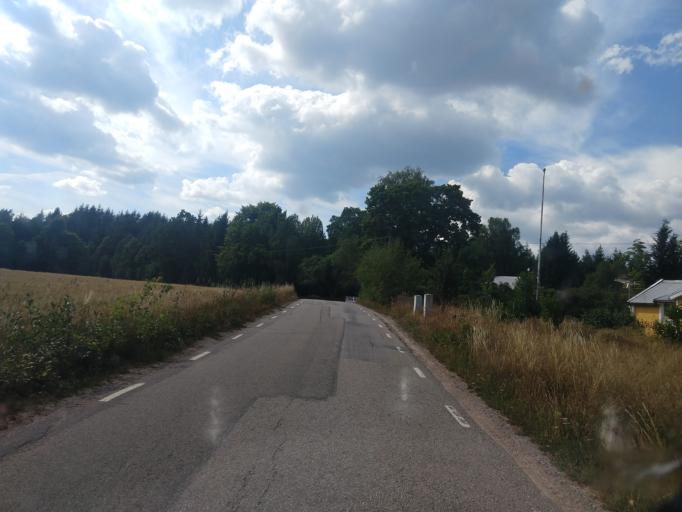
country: SE
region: Blekinge
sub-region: Karlskrona Kommun
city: Nattraby
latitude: 56.2572
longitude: 15.5223
